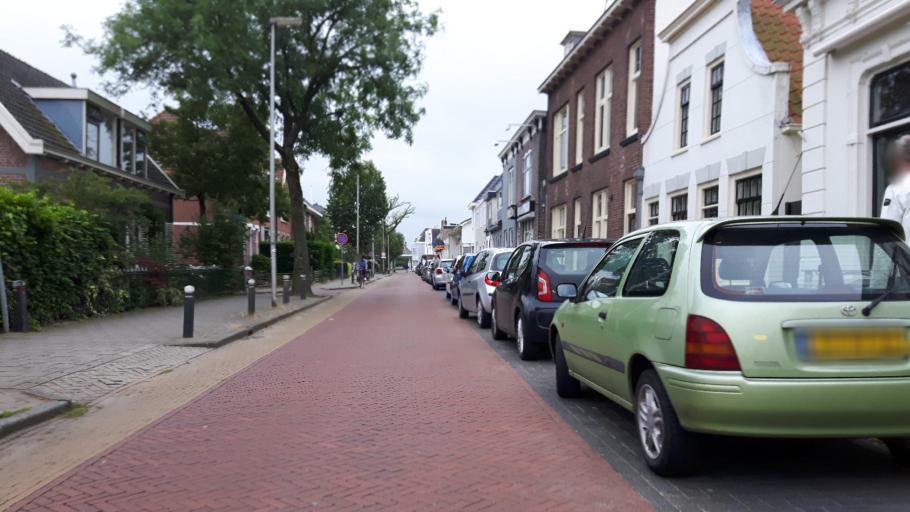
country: NL
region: South Holland
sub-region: Gemeente Alphen aan den Rijn
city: Alphen aan den Rijn
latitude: 52.1369
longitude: 4.6636
